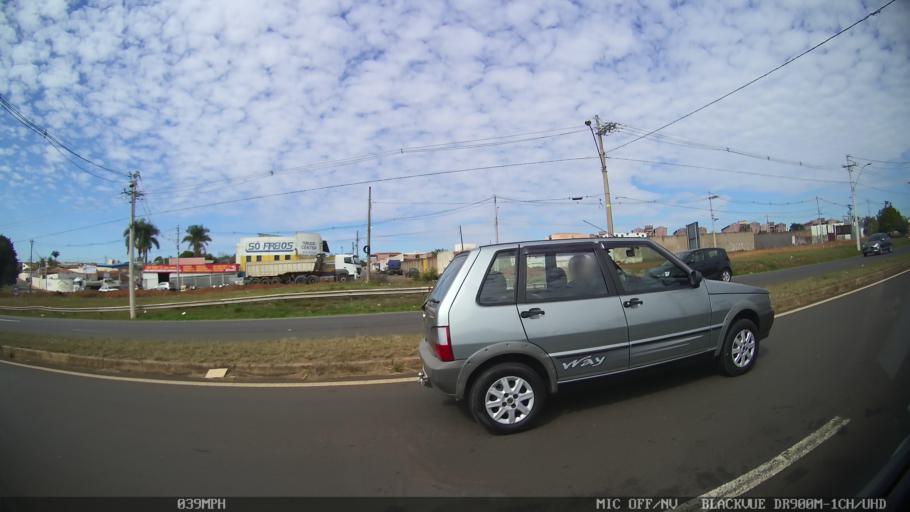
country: BR
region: Sao Paulo
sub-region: Santa Barbara D'Oeste
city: Santa Barbara d'Oeste
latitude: -22.7692
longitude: -47.4214
